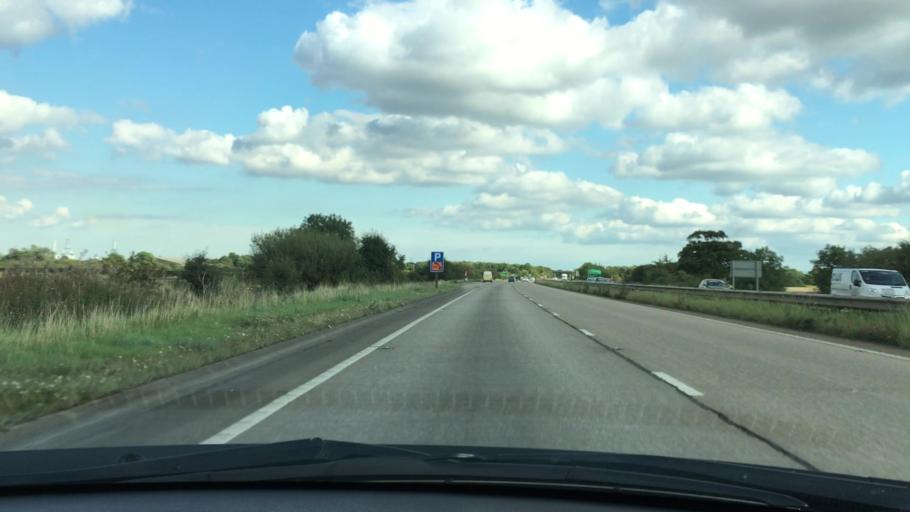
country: GB
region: England
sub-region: North East Lincolnshire
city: Healing
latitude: 53.5960
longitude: -0.1846
